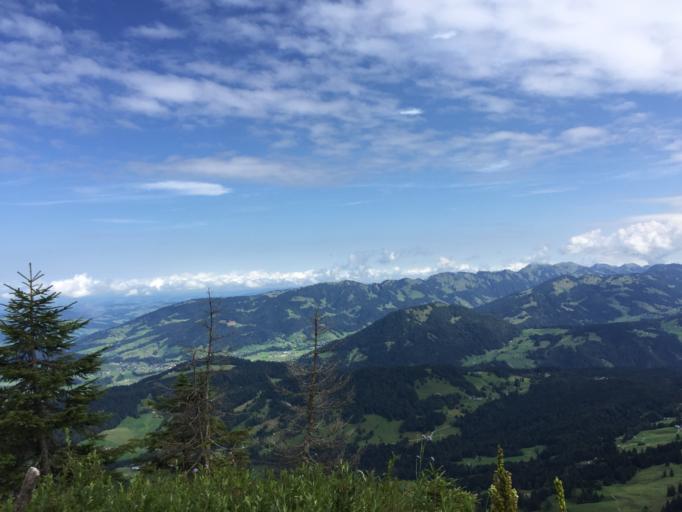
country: AT
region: Vorarlberg
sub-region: Politischer Bezirk Bregenz
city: Bizau
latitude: 47.4027
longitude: 9.9459
